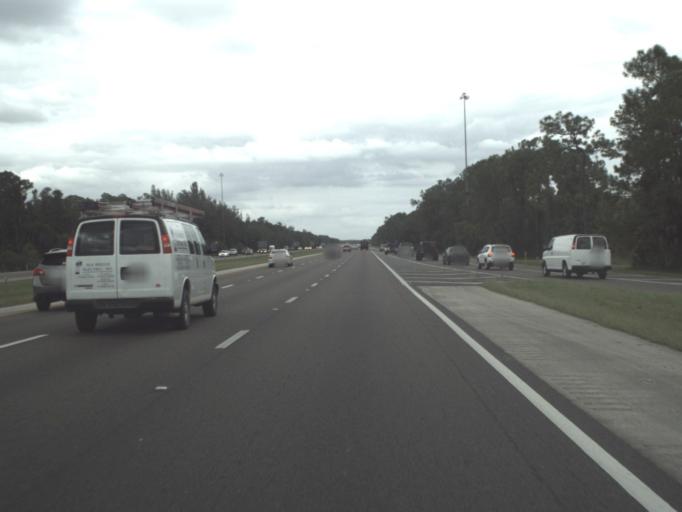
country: US
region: Florida
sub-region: Collier County
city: Vineyards
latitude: 26.2162
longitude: -81.7360
